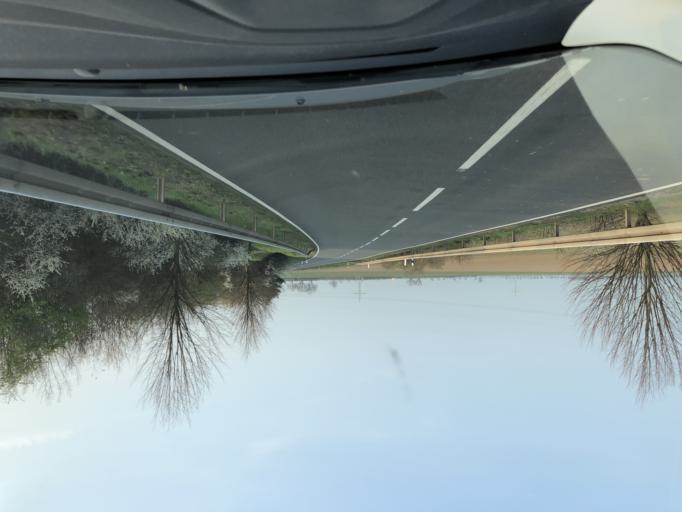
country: DE
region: Saxony-Anhalt
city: Brehna
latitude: 51.5555
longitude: 12.2306
